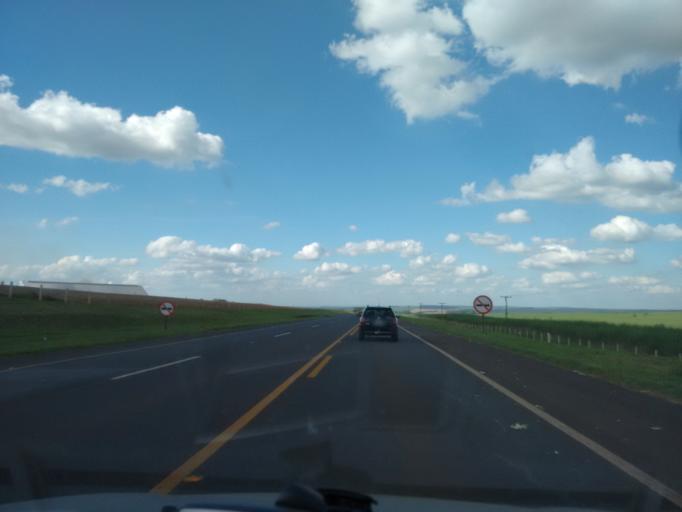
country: BR
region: Sao Paulo
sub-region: Americo Brasiliense
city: Americo Brasiliense
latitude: -21.7662
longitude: -48.0857
